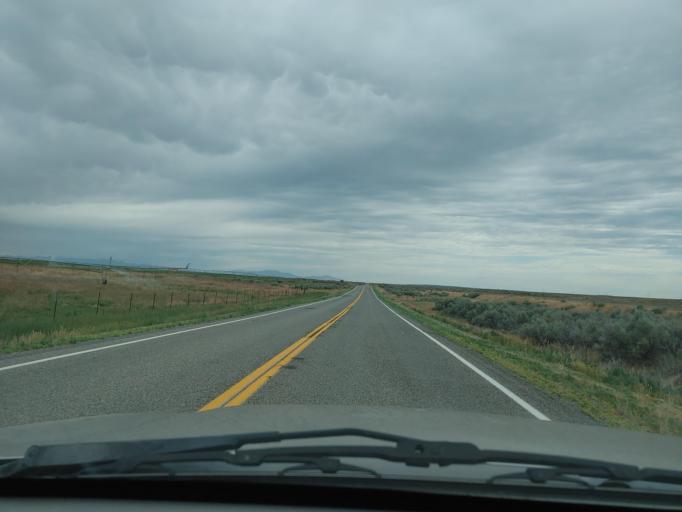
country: US
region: Idaho
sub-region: Lincoln County
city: Shoshone
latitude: 43.0587
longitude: -114.1302
